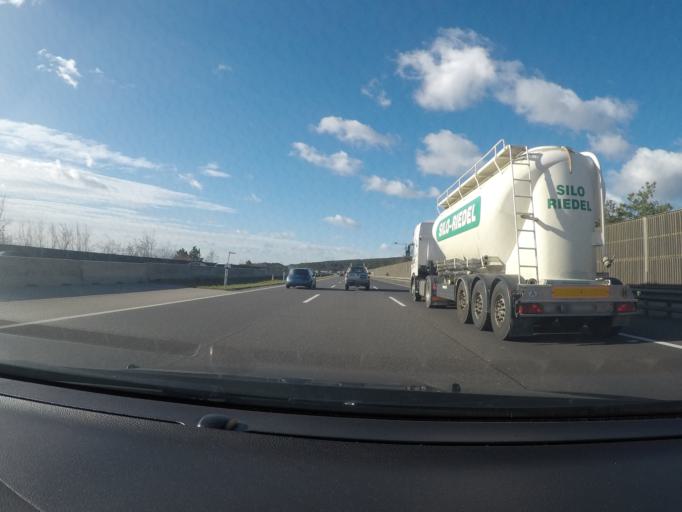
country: AT
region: Lower Austria
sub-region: Politischer Bezirk Wiener Neustadt
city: Theresienfeld
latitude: 47.8656
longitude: 16.1902
